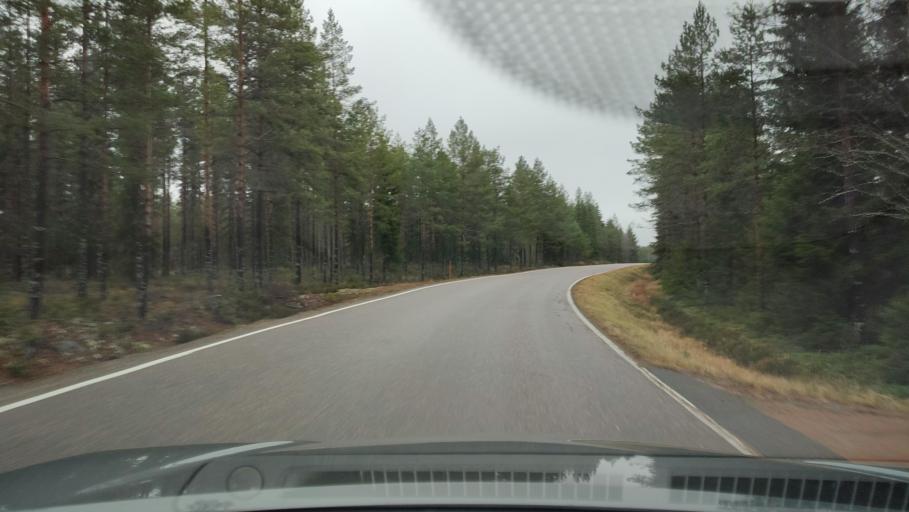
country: FI
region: Southern Ostrobothnia
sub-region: Suupohja
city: Isojoki
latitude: 62.2200
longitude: 21.9942
